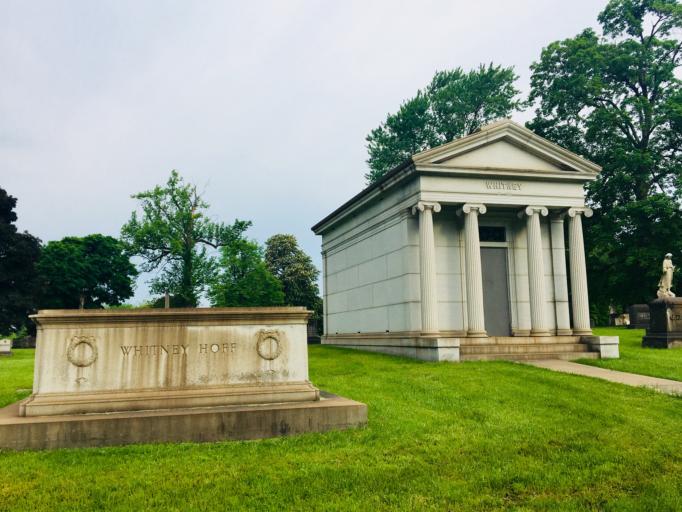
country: US
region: Michigan
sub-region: Wayne County
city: River Rouge
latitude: 42.2982
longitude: -83.1371
